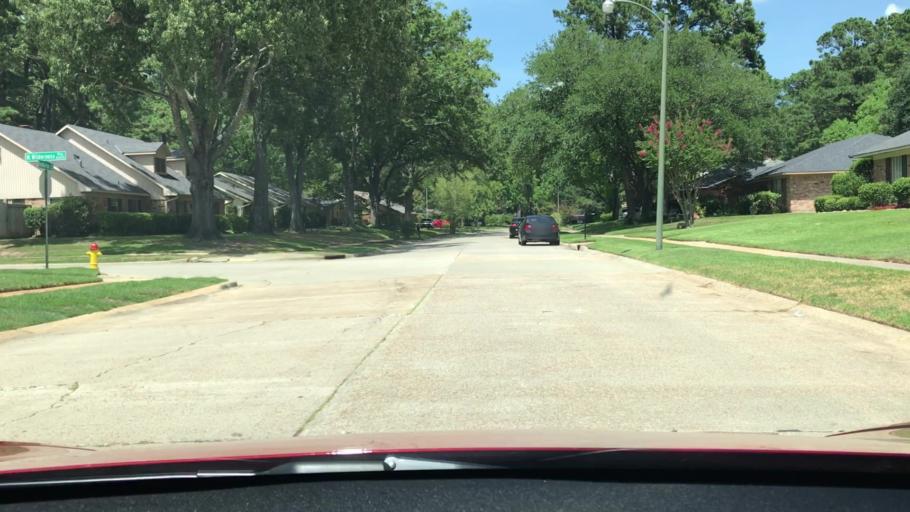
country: US
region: Louisiana
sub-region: Bossier Parish
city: Bossier City
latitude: 32.4221
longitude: -93.7355
